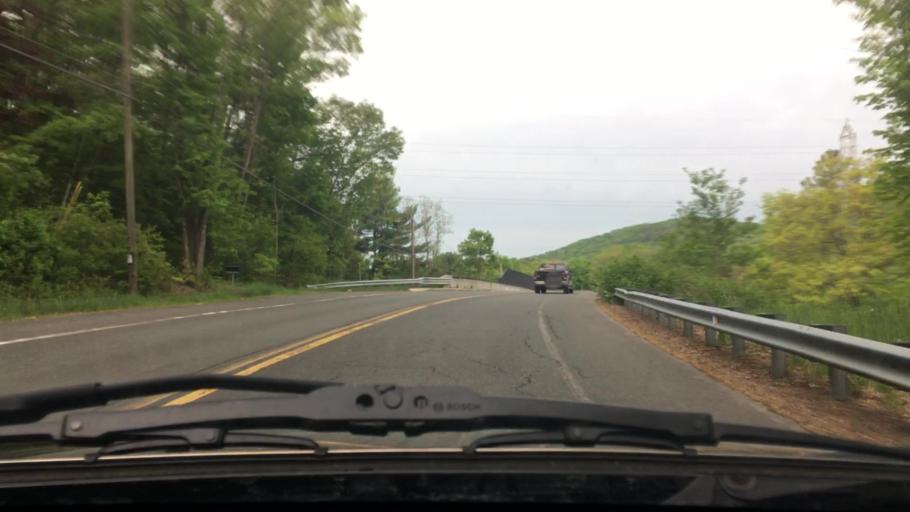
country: US
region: Massachusetts
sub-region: Franklin County
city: Leverett
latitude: 42.4575
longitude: -72.5218
